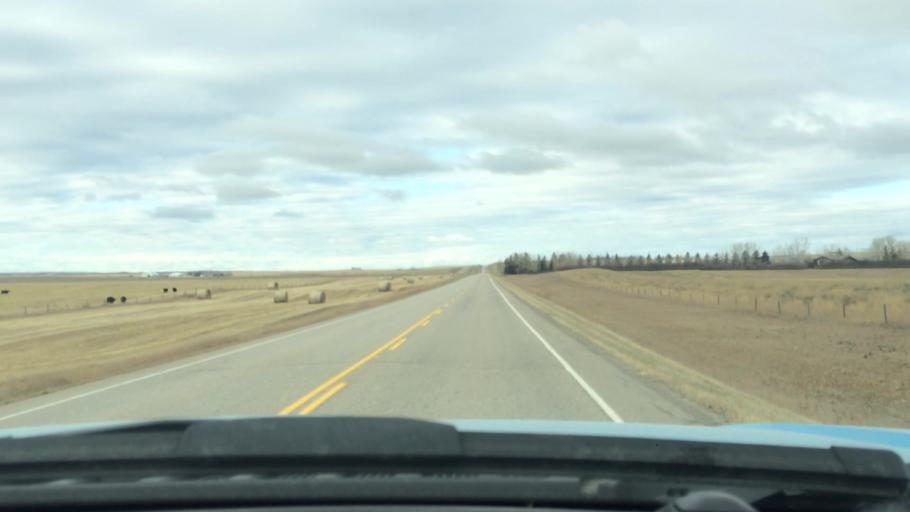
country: CA
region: Alberta
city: Airdrie
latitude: 51.2125
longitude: -114.0841
